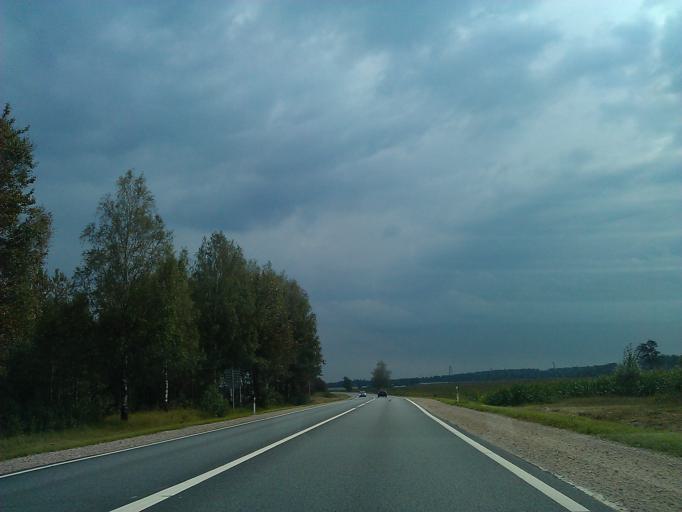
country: LV
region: Lecava
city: Iecava
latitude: 56.5141
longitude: 24.1728
